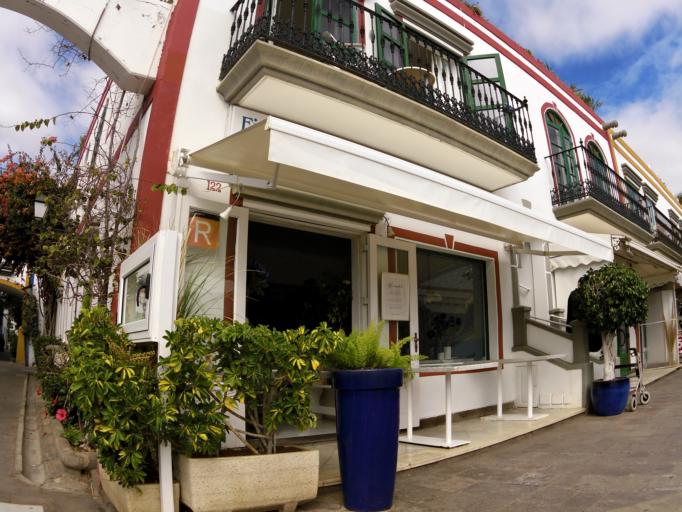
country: ES
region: Canary Islands
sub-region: Provincia de Las Palmas
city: Puerto Rico
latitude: 27.8174
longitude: -15.7647
